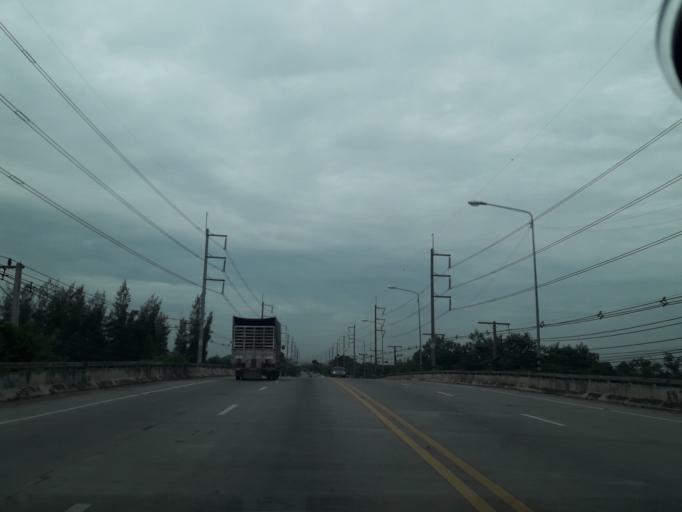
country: TH
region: Pathum Thani
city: Ban Lam Luk Ka
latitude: 13.9509
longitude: 100.8165
